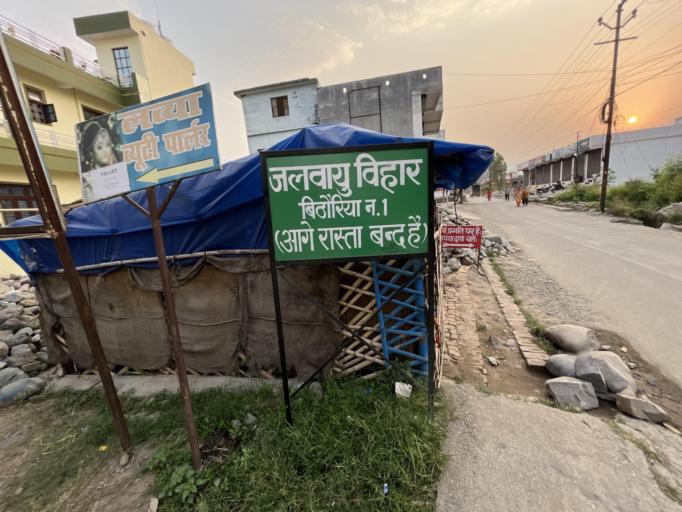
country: IN
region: Uttarakhand
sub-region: Naini Tal
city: Haldwani
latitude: 29.2307
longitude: 79.5054
